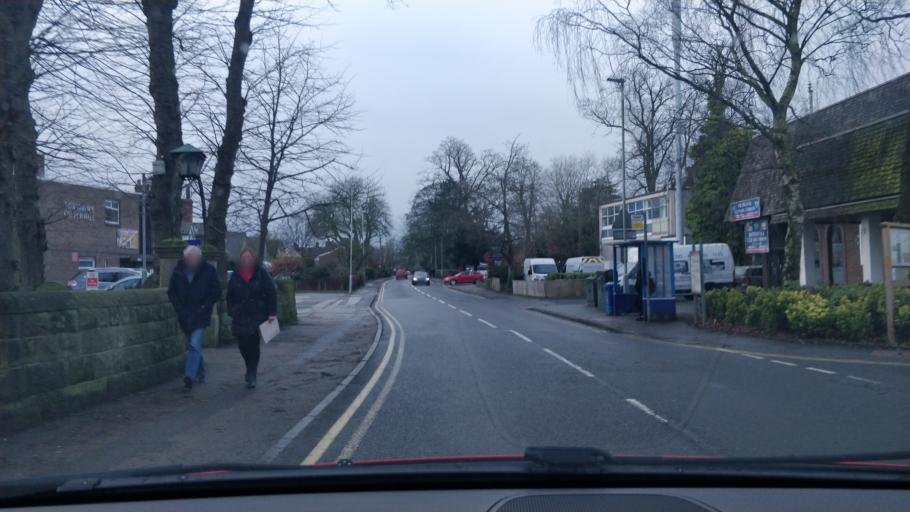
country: GB
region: England
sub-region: Lancashire
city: Croston
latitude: 53.7270
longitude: -2.7825
